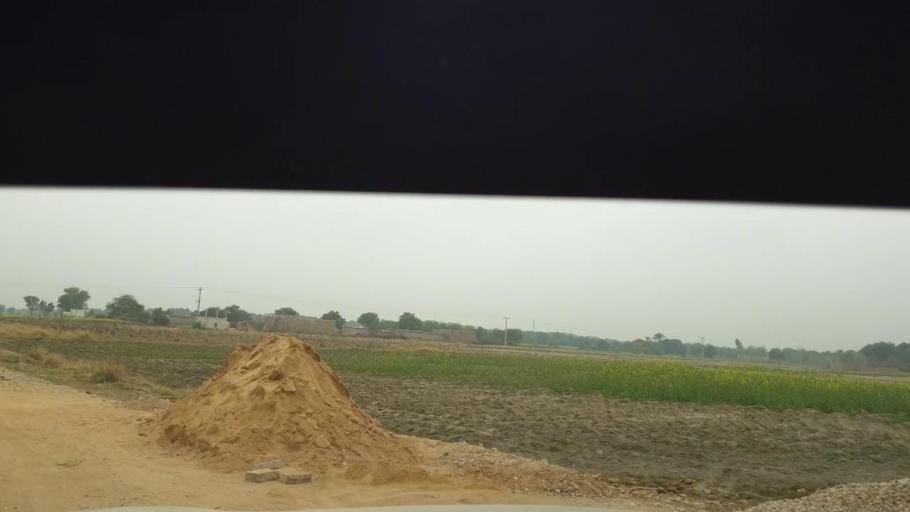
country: PK
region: Sindh
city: Berani
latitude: 25.7691
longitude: 68.7646
